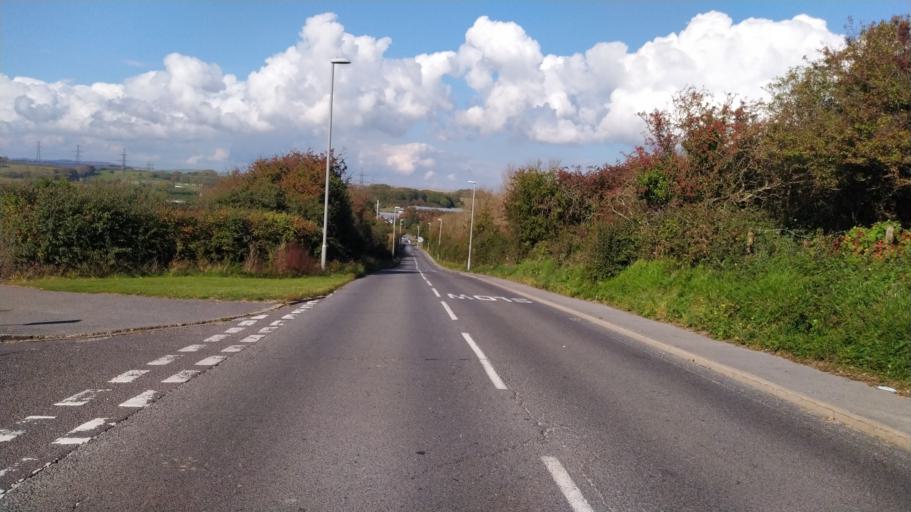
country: GB
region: England
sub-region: Dorset
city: Chickerell
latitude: 50.6156
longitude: -2.4823
